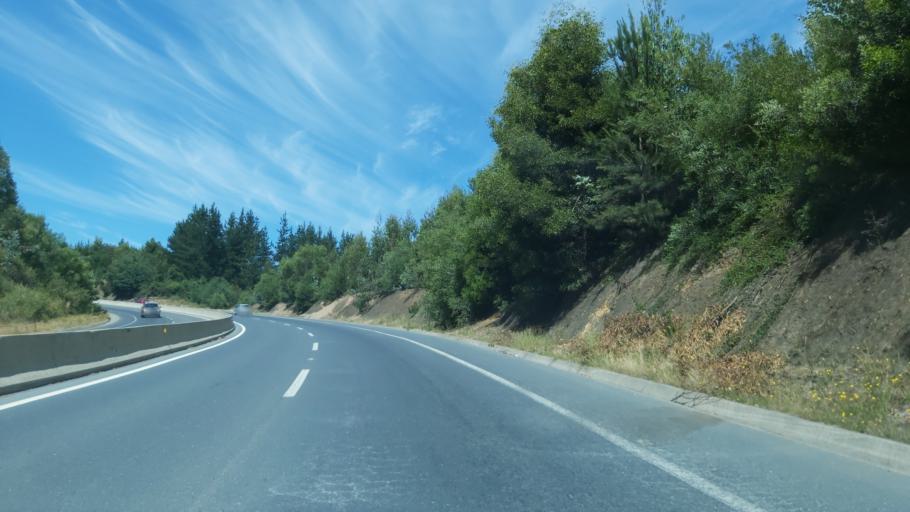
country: CL
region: Biobio
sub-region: Provincia de Concepcion
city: Lota
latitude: -37.0829
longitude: -73.1385
